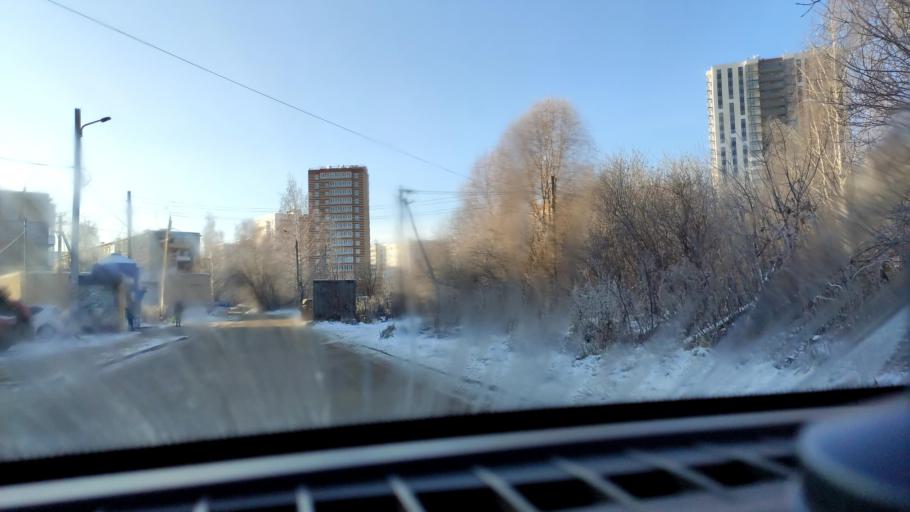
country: RU
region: Perm
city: Kondratovo
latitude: 58.0309
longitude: 56.0261
